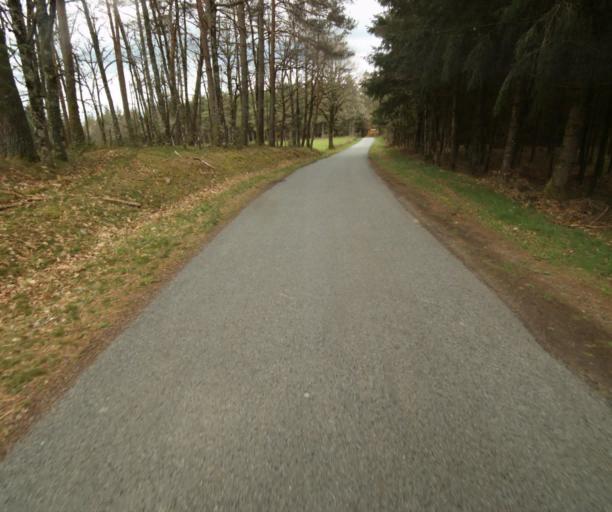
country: FR
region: Limousin
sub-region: Departement de la Correze
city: Correze
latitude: 45.3310
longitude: 1.9354
